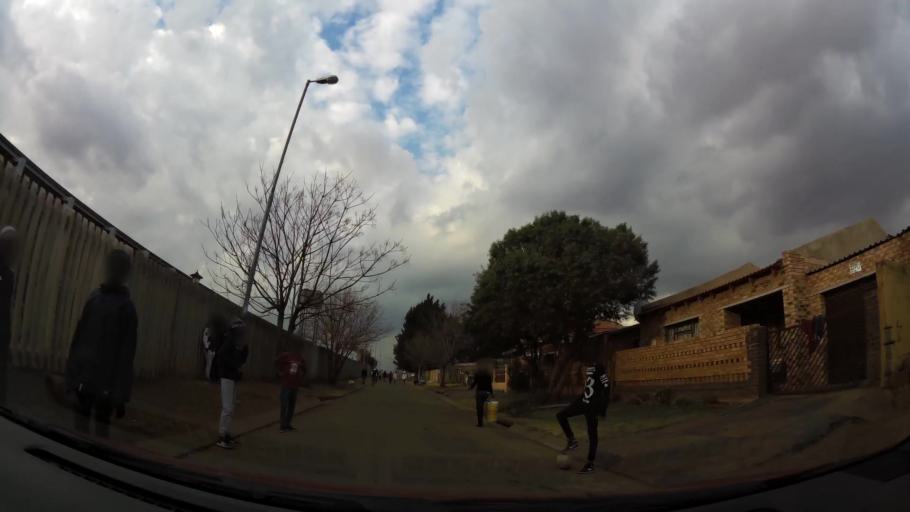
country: ZA
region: Gauteng
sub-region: City of Johannesburg Metropolitan Municipality
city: Soweto
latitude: -26.2398
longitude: 27.8231
